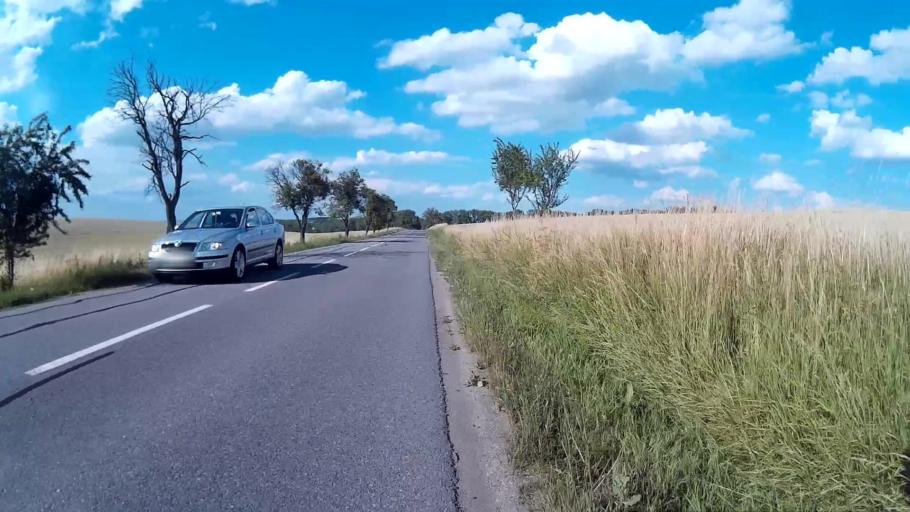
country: CZ
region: South Moravian
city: Sitborice
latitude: 49.0225
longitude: 16.7787
